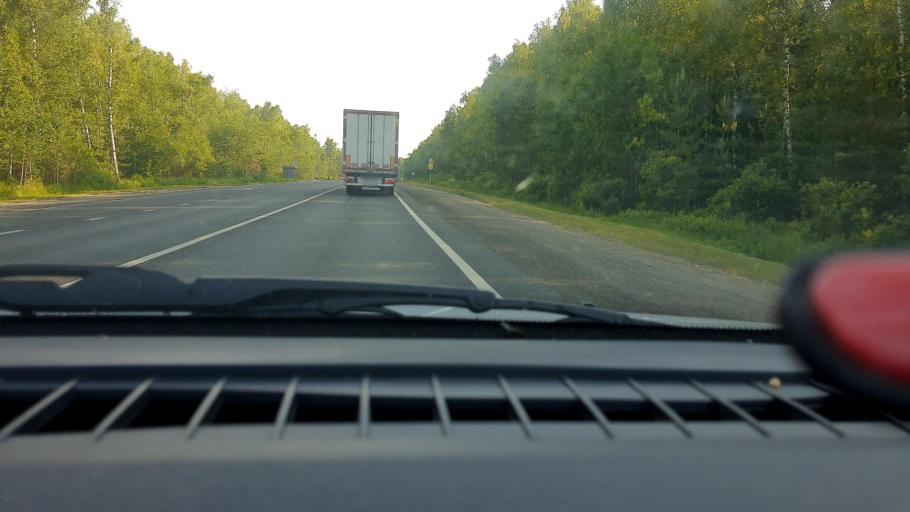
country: RU
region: Nizjnij Novgorod
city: Arzamas
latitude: 55.4836
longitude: 43.8862
